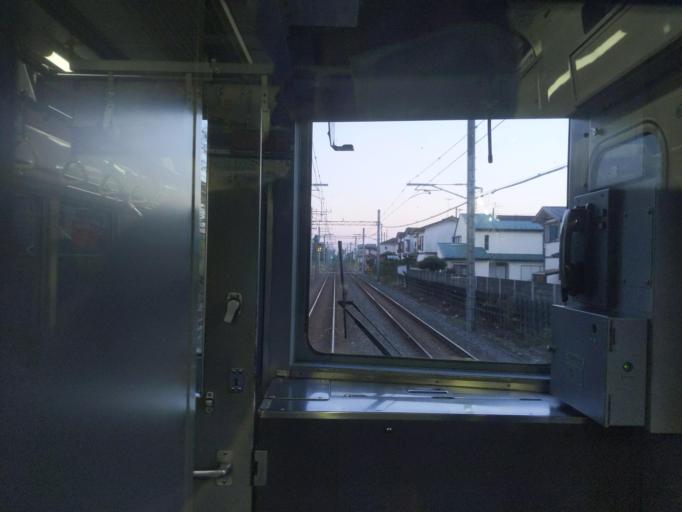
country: JP
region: Chiba
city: Nagareyama
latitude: 35.9070
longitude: 139.9073
